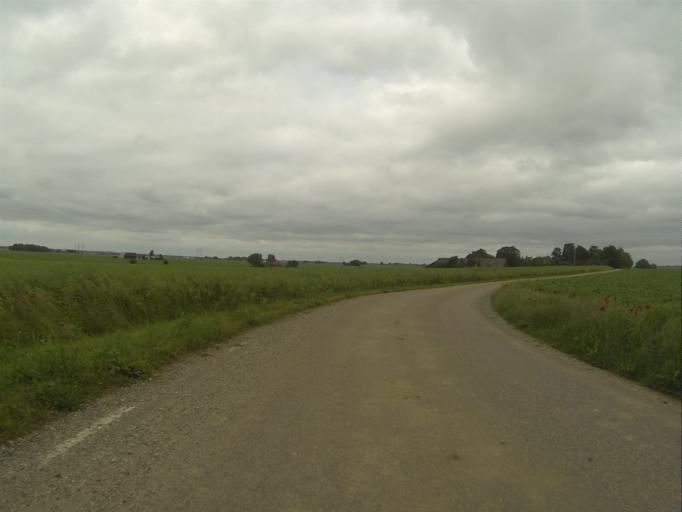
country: SE
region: Skane
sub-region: Staffanstorps Kommun
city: Staffanstorp
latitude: 55.6784
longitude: 13.2658
